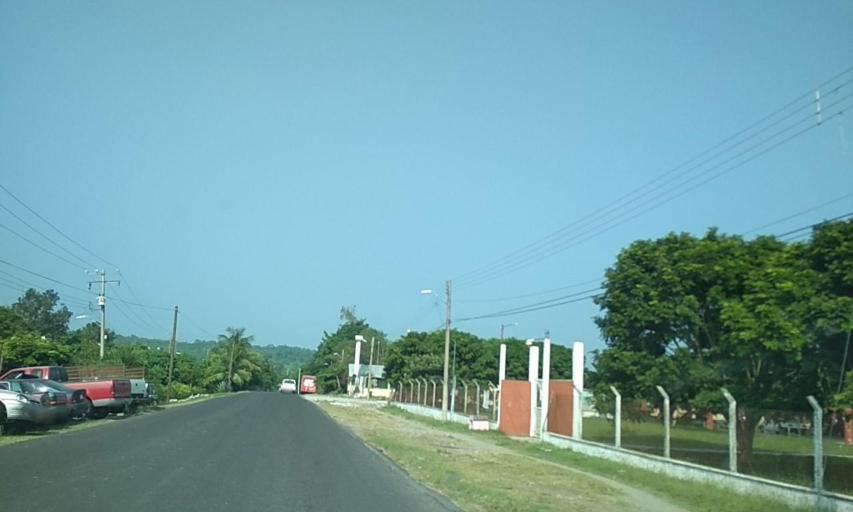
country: MX
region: Veracruz
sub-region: Misantla
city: La Defensa
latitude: 20.0512
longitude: -96.9879
